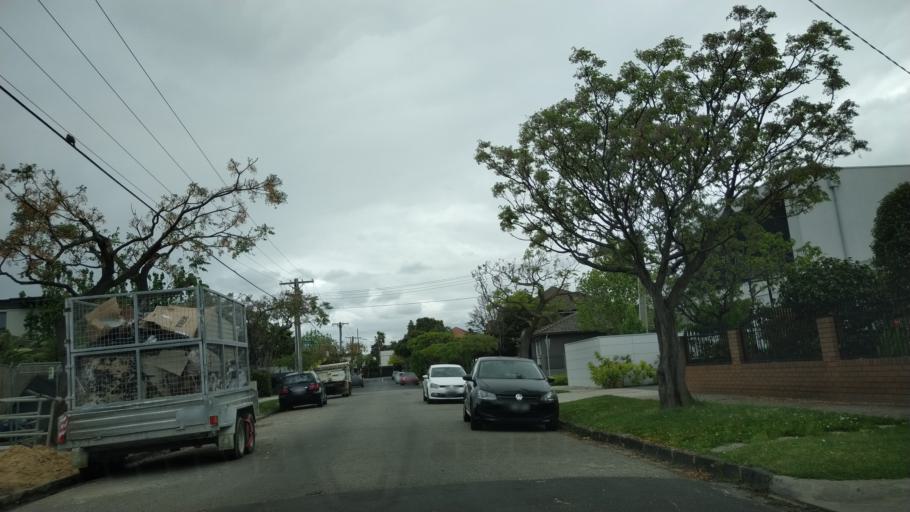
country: AU
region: Victoria
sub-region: Glen Eira
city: Caulfield
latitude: -37.8819
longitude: 145.0259
